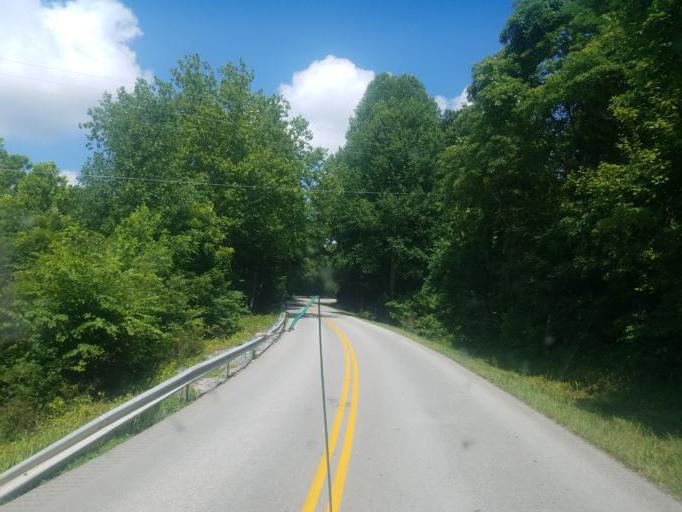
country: US
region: Kentucky
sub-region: Hart County
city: Munfordville
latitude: 37.3167
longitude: -86.0863
